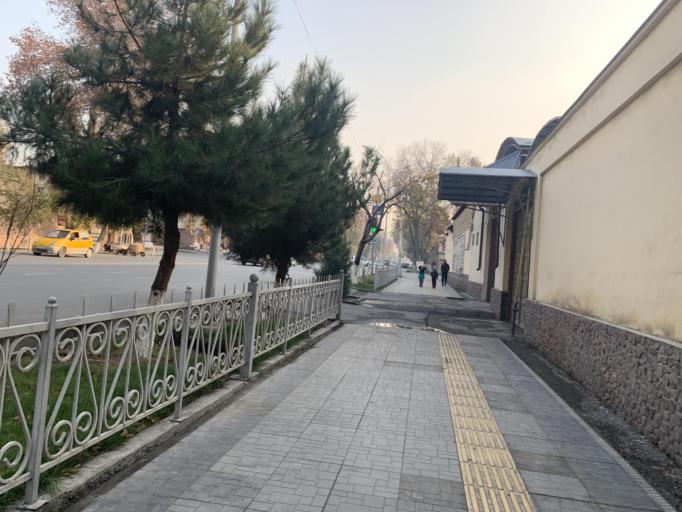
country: UZ
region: Fergana
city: Qo`qon
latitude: 40.5315
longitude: 70.9381
